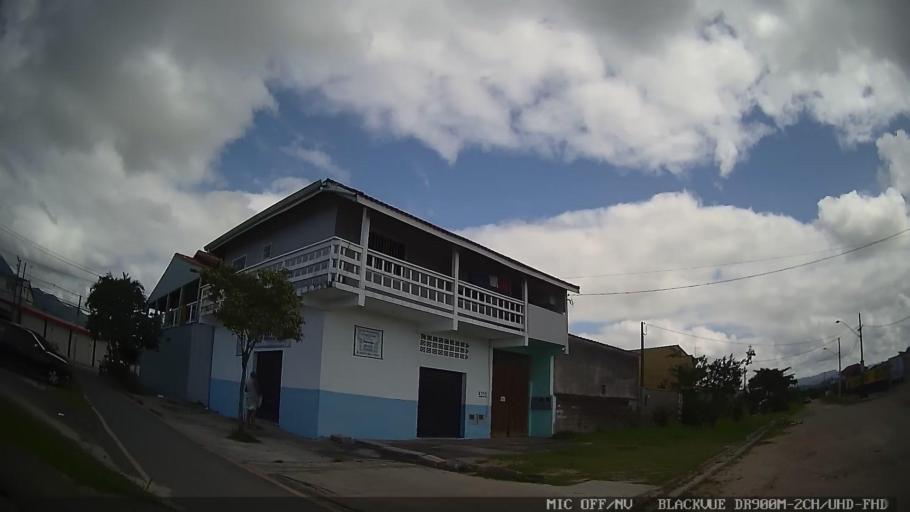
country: BR
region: Sao Paulo
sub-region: Peruibe
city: Peruibe
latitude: -24.3105
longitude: -47.0109
